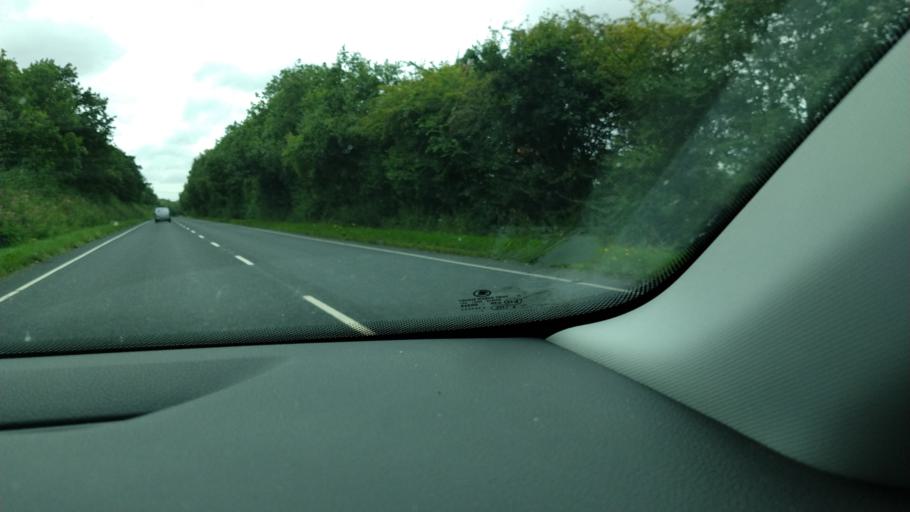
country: GB
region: England
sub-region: East Riding of Yorkshire
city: Barmby on the Marsh
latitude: 53.7214
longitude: -0.9781
